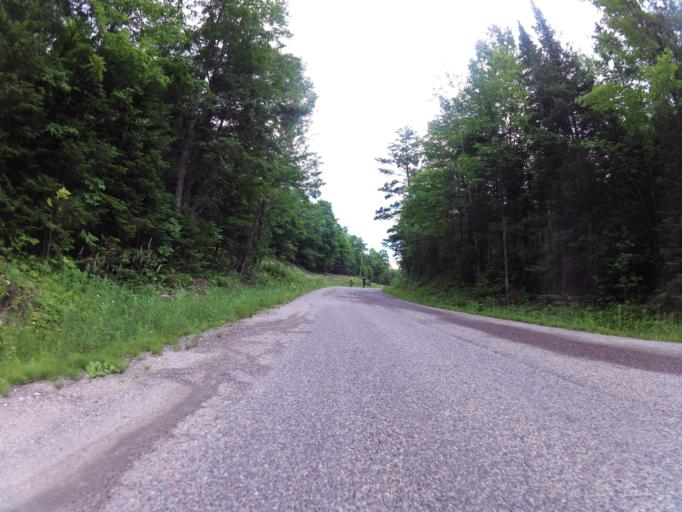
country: CA
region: Ontario
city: Renfrew
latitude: 45.0372
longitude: -76.7220
